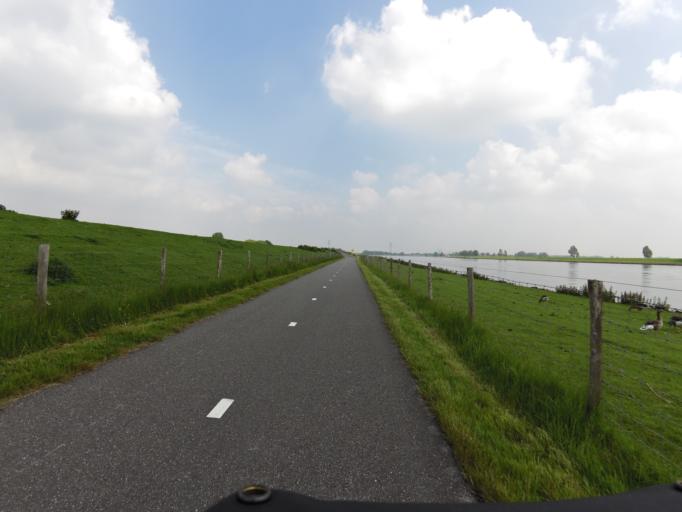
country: NL
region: South Holland
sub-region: Gemeente Spijkenisse
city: Spijkenisse
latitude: 51.8113
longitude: 4.3128
